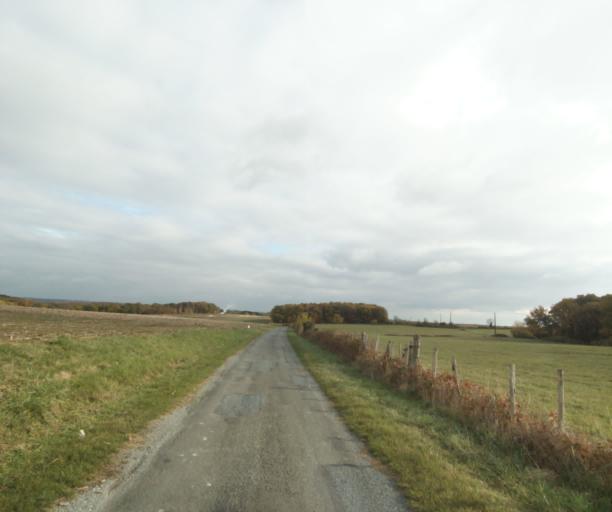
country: FR
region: Poitou-Charentes
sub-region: Departement de la Charente-Maritime
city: Saint-Georges-des-Coteaux
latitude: 45.7641
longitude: -0.6824
